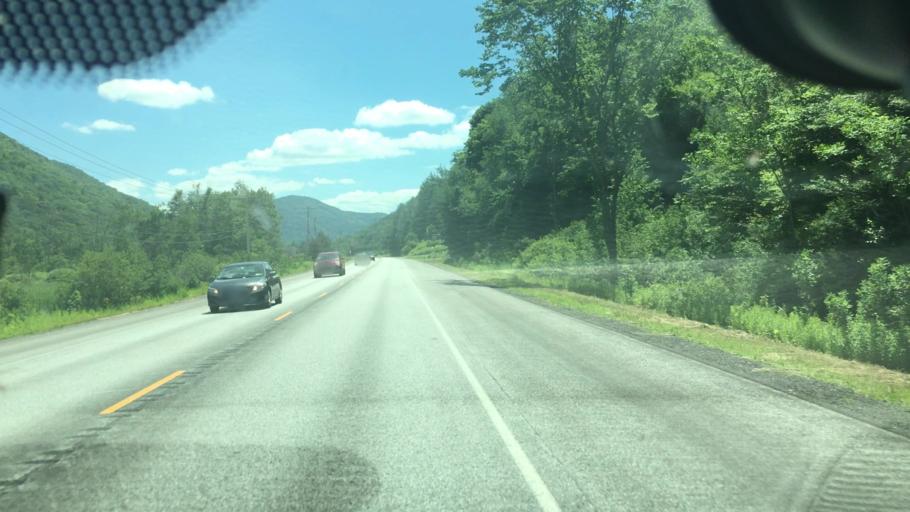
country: US
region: Vermont
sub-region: Rutland County
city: Rutland
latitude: 43.6437
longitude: -72.7675
